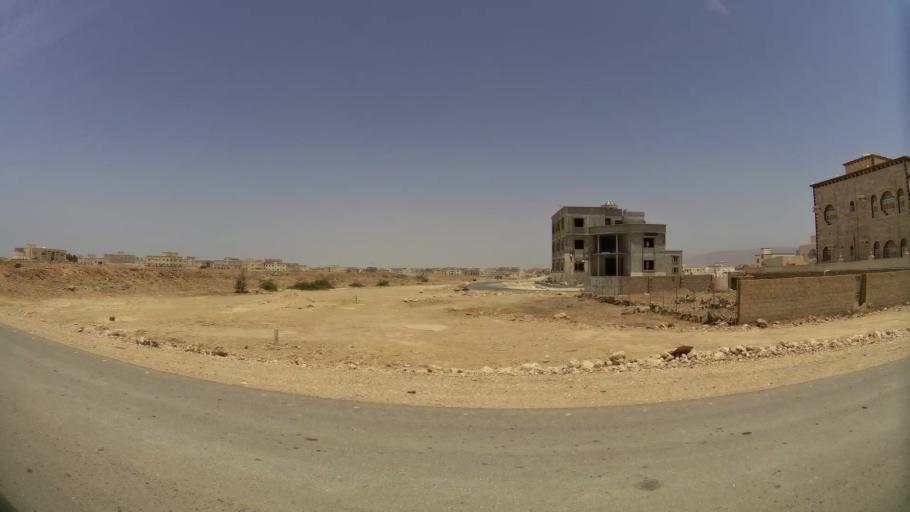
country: OM
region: Zufar
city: Salalah
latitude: 17.0967
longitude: 54.1685
